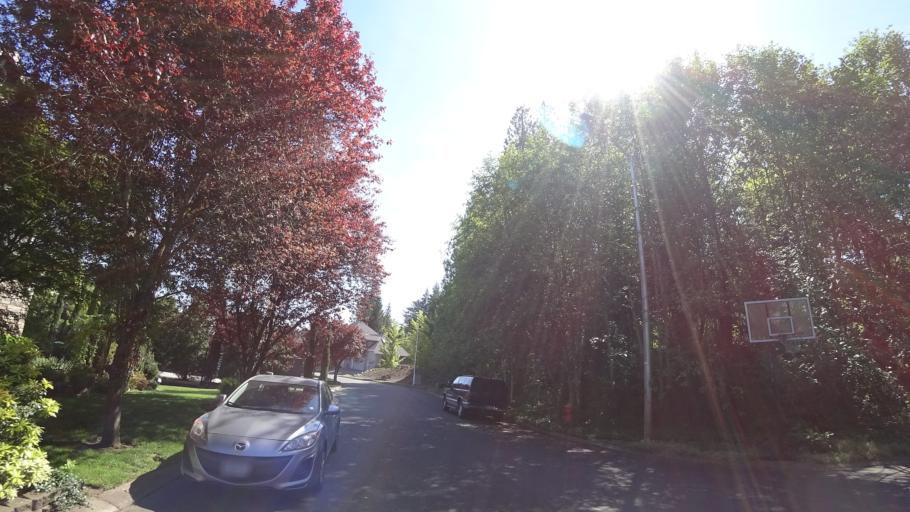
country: US
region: Oregon
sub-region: Washington County
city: Raleigh Hills
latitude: 45.4920
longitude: -122.7411
